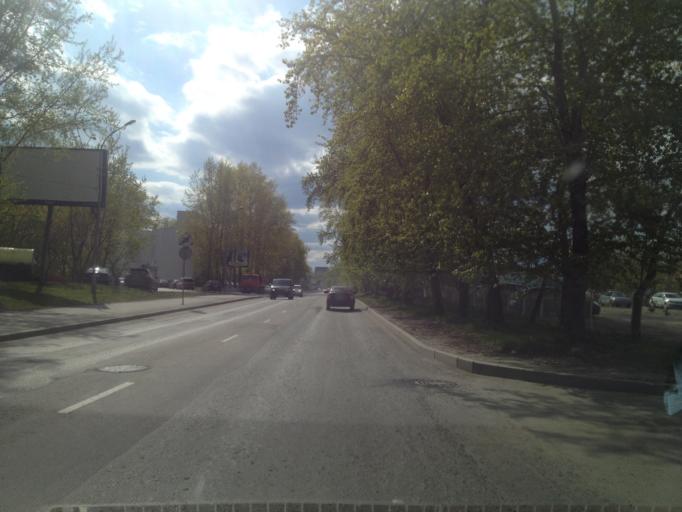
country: RU
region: Sverdlovsk
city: Yekaterinburg
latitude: 56.8576
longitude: 60.5637
